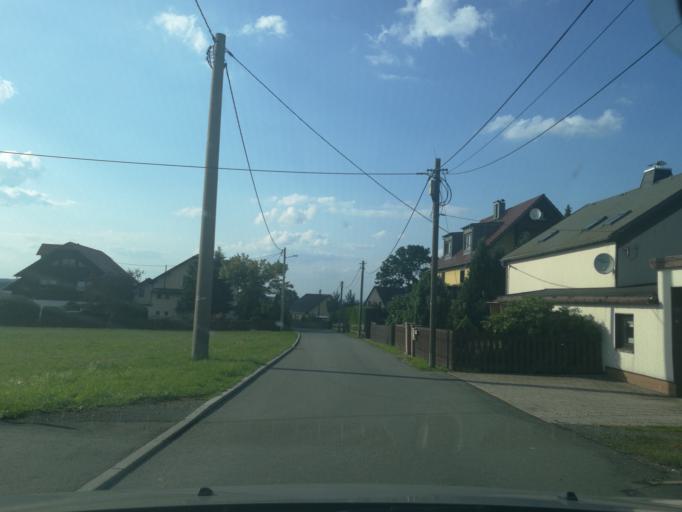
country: DE
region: Saxony
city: Adorf
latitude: 50.3069
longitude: 12.2746
